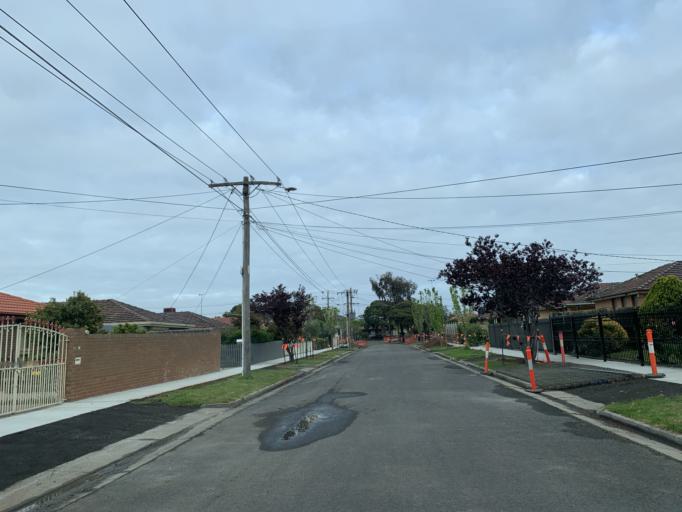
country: AU
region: Victoria
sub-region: Brimbank
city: Kealba
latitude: -37.7492
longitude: 144.8222
